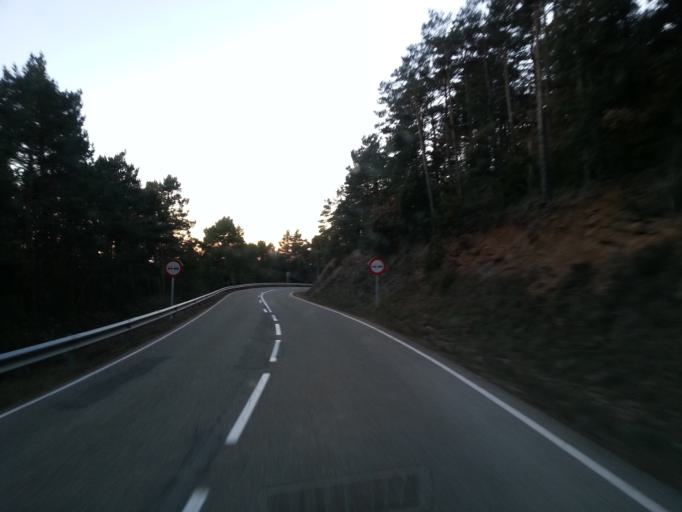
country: ES
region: Catalonia
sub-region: Provincia de Lleida
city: Olius
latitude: 42.0930
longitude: 1.5315
